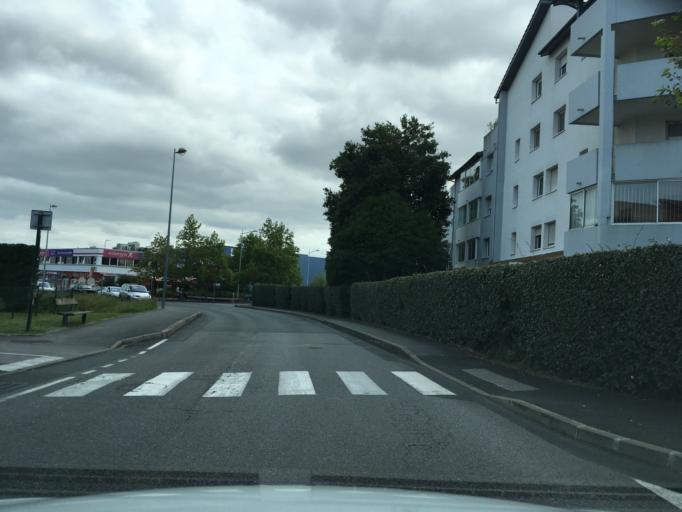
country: FR
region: Aquitaine
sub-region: Departement des Pyrenees-Atlantiques
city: Anglet
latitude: 43.4835
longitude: -1.5085
